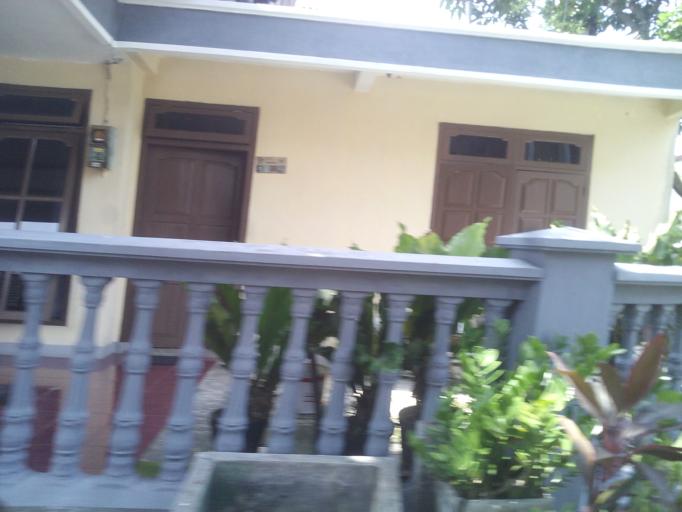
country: ID
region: East Java
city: Sumbersari Wetan
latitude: -8.1790
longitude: 113.7182
